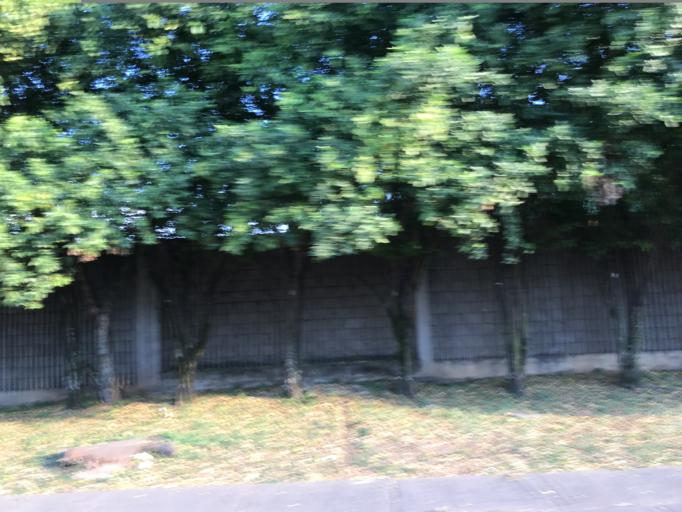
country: CO
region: Valle del Cauca
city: Cali
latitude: 3.4910
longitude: -76.5054
